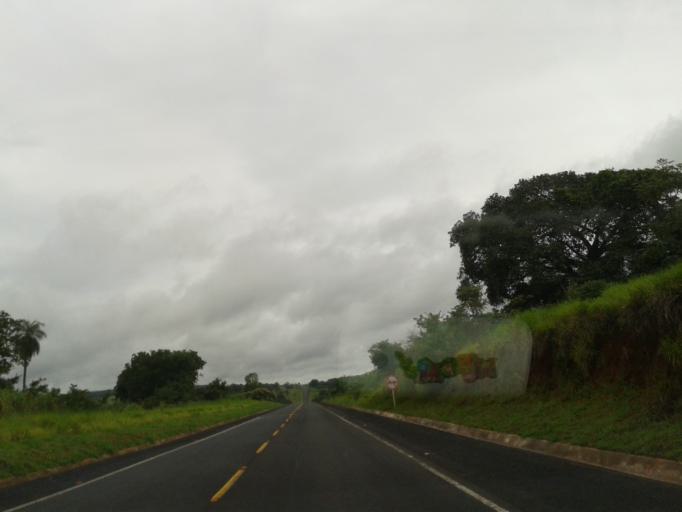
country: BR
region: Minas Gerais
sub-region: Santa Vitoria
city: Santa Vitoria
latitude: -19.2481
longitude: -50.0125
